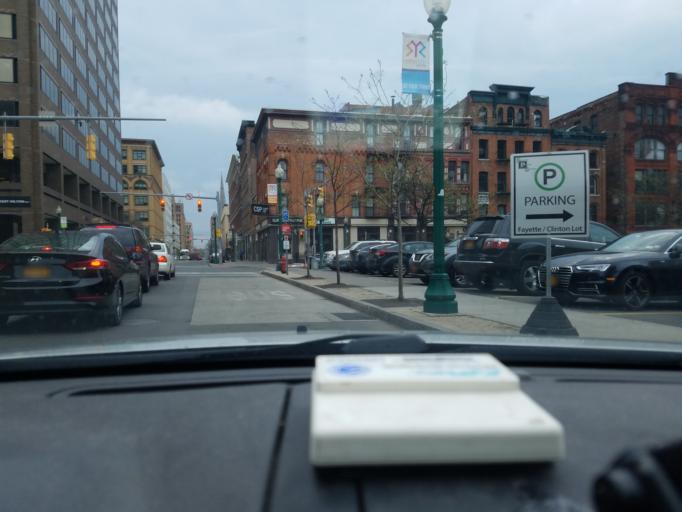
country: US
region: New York
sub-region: Onondaga County
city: Syracuse
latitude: 43.0487
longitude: -76.1541
